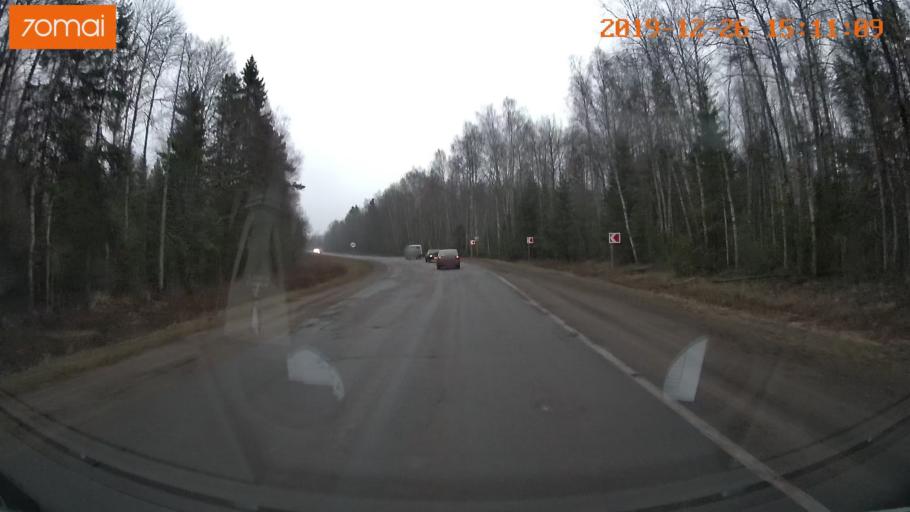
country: RU
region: Jaroslavl
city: Rybinsk
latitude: 58.1358
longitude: 38.8580
